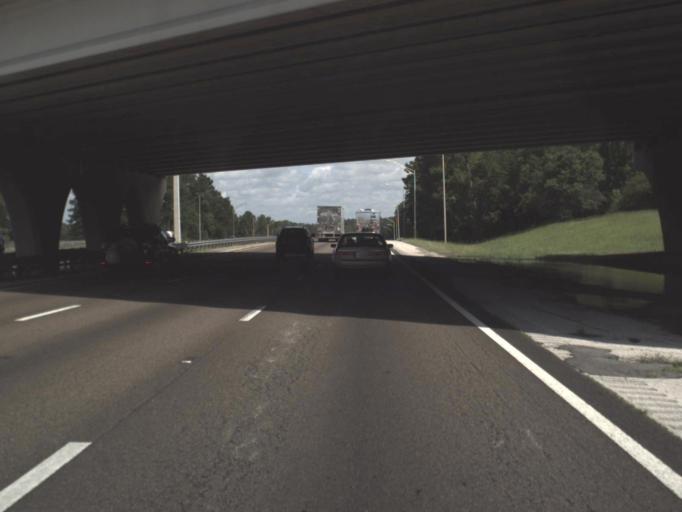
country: US
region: Florida
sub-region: Alachua County
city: Alachua
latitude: 29.6887
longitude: -82.4461
